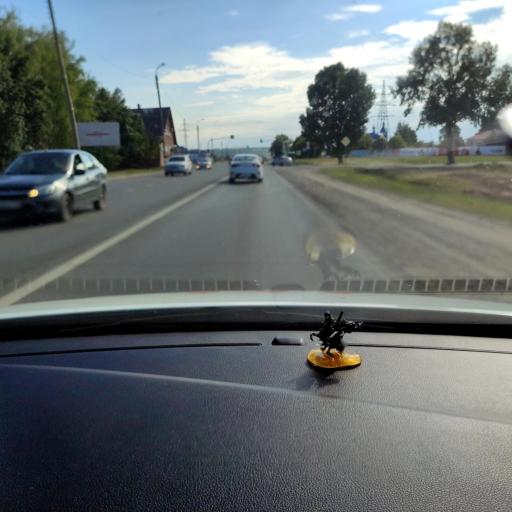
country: RU
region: Tatarstan
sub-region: Zelenodol'skiy Rayon
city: Zelenodolsk
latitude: 55.8473
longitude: 48.5546
